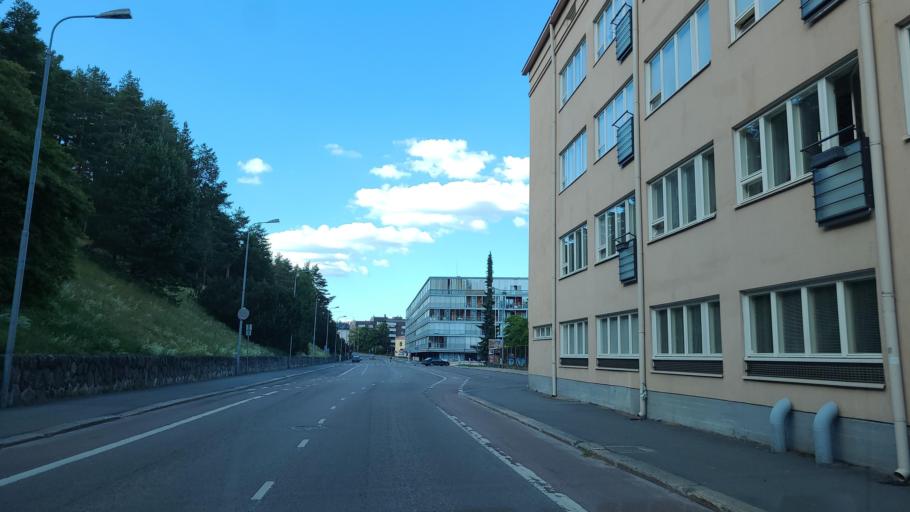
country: FI
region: Central Finland
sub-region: Jyvaeskylae
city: Jyvaeskylae
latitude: 62.2435
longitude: 25.7429
